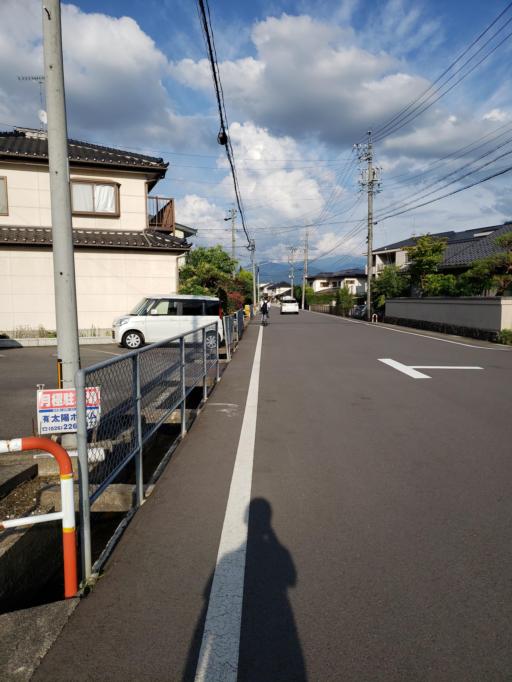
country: JP
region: Nagano
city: Nagano-shi
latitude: 36.6282
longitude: 138.1619
